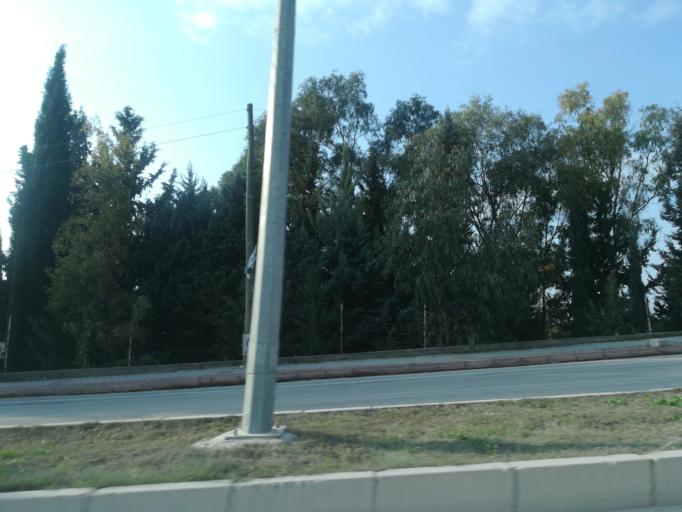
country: TR
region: Adana
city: Adana
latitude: 37.0671
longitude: 35.3750
